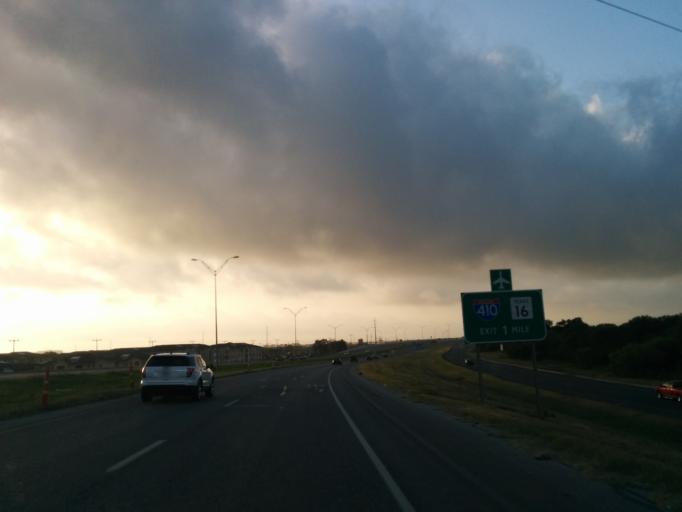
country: US
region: Texas
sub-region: Bexar County
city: Leon Valley
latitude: 29.4462
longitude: -98.6696
